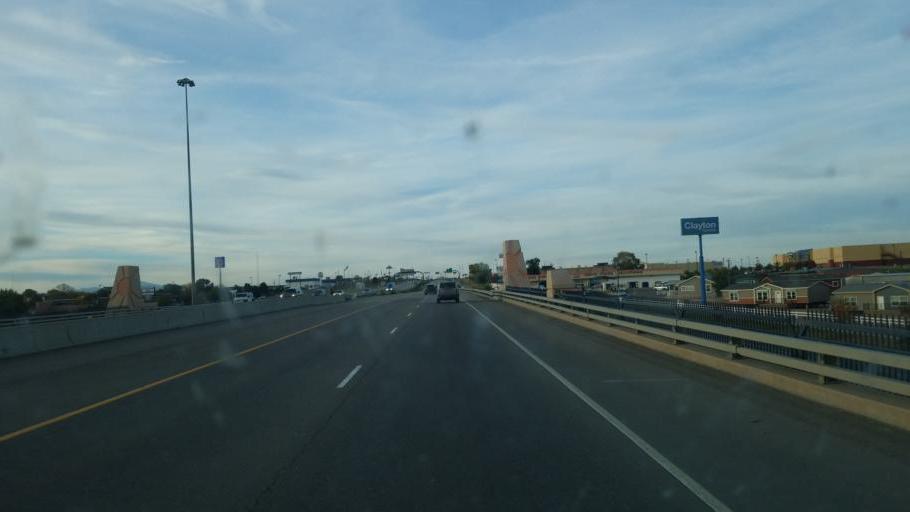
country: US
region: Colorado
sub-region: Pueblo County
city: Pueblo
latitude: 38.3074
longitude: -104.6136
